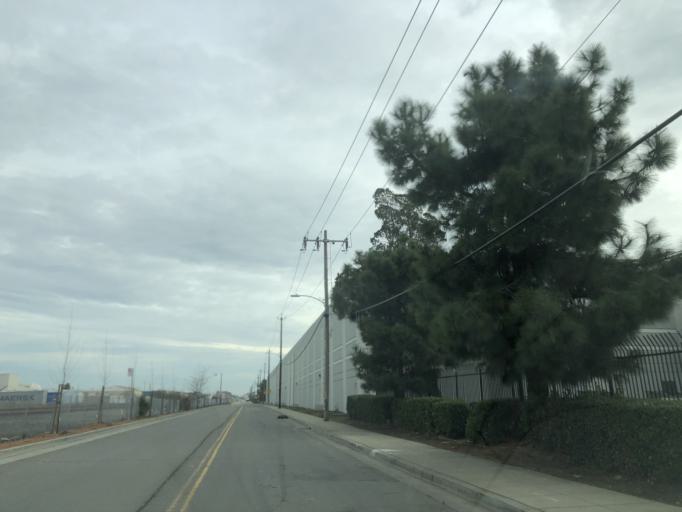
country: US
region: California
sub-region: Alameda County
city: San Leandro
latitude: 37.7452
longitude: -122.1905
